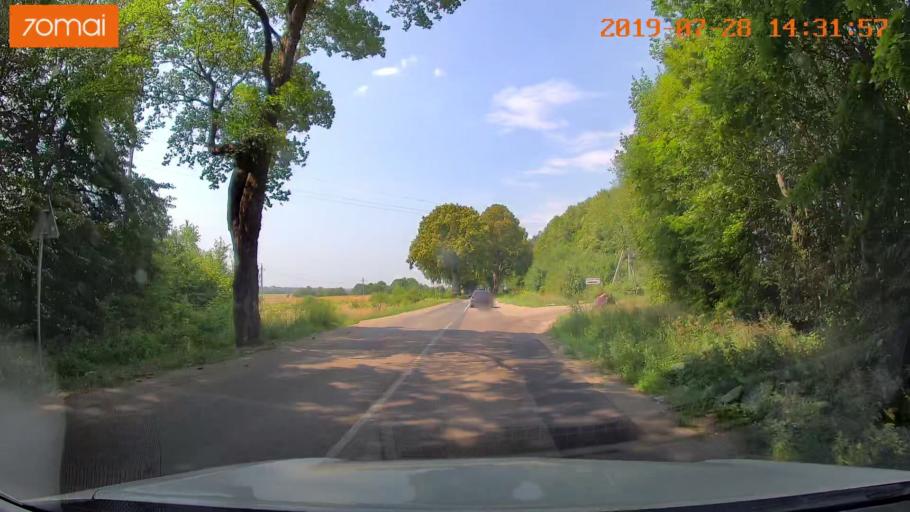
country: RU
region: Kaliningrad
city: Primorsk
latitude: 54.8095
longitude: 20.0467
